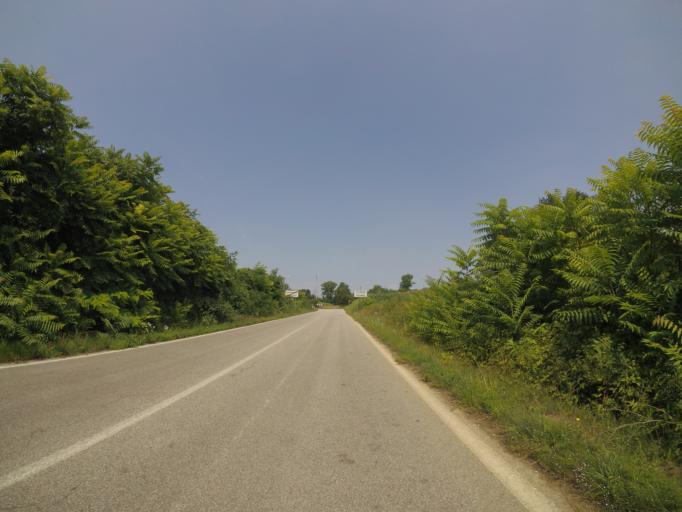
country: IT
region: Friuli Venezia Giulia
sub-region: Provincia di Udine
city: Basiliano-Vissandone
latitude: 46.0231
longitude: 13.1006
